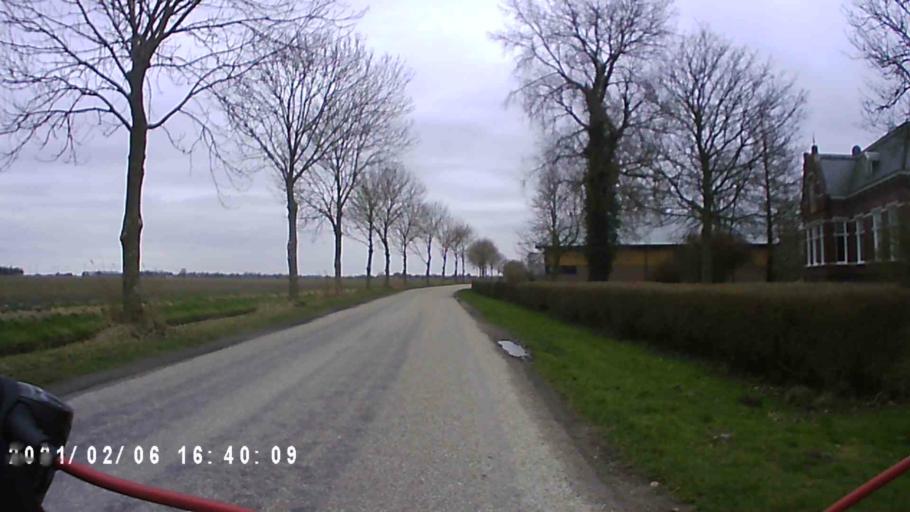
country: NL
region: Groningen
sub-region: Gemeente Bedum
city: Bedum
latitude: 53.4190
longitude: 6.7081
